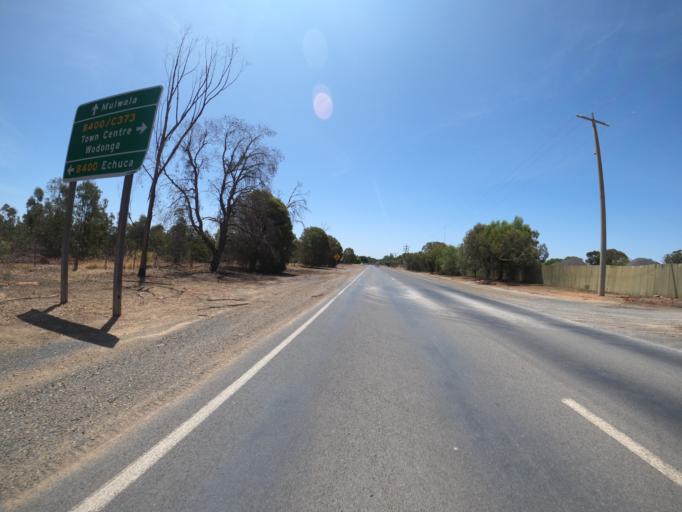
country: AU
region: Victoria
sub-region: Moira
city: Yarrawonga
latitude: -36.0232
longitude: 145.9955
